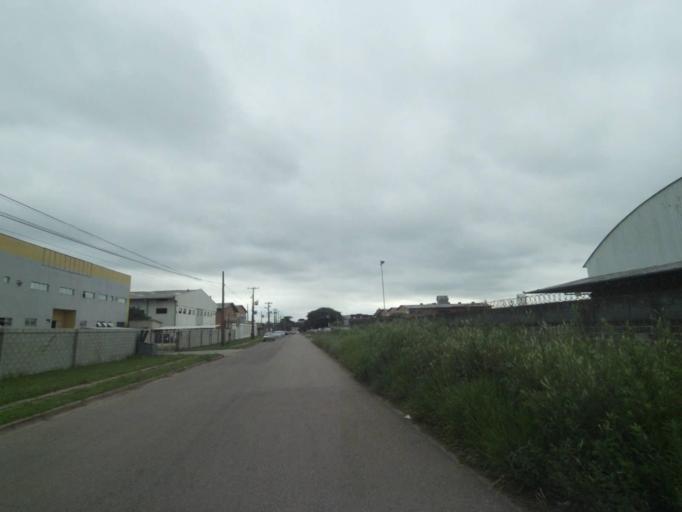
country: BR
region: Parana
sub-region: Curitiba
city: Curitiba
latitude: -25.5205
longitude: -49.3232
